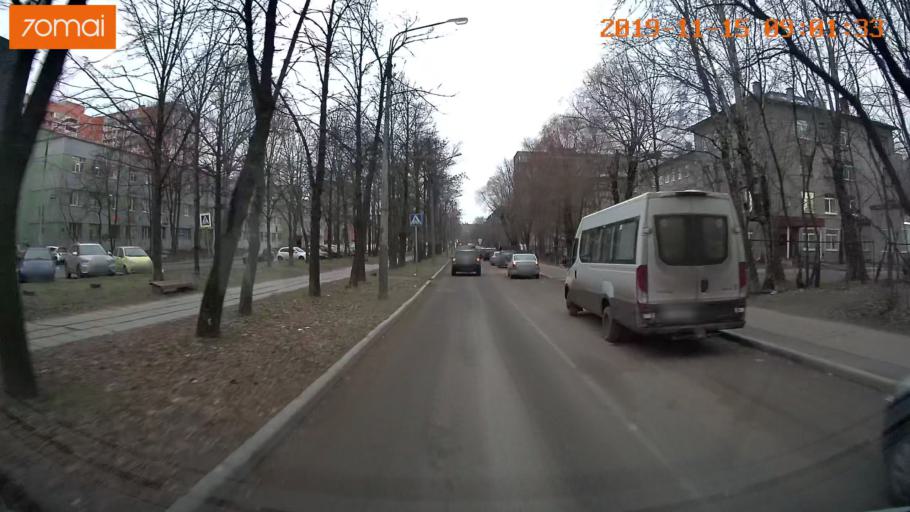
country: RU
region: Vologda
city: Cherepovets
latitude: 59.1328
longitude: 37.9261
